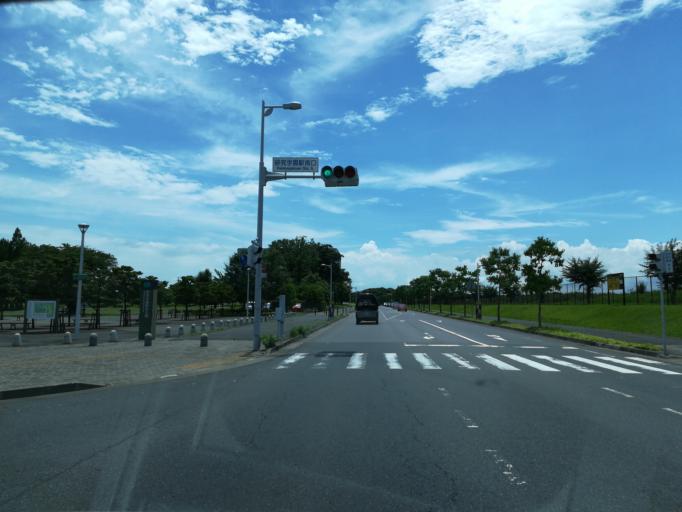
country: JP
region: Ibaraki
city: Naka
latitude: 36.0821
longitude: 140.0795
